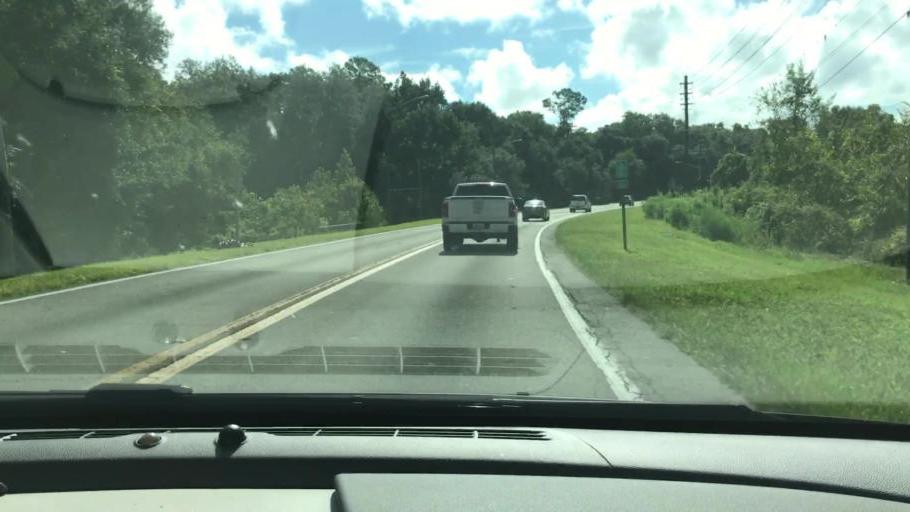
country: US
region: Florida
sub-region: Alachua County
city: Gainesville
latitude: 29.6494
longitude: -82.4045
